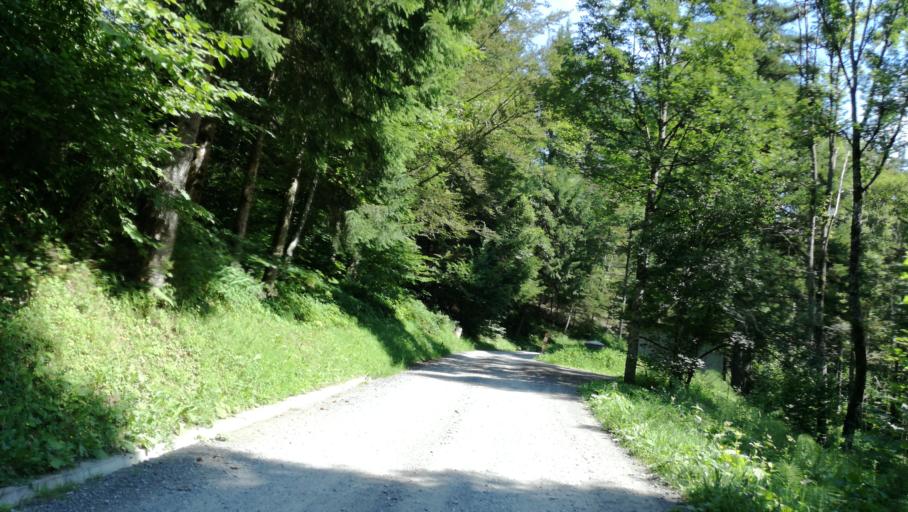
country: CH
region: Zug
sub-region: Zug
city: Unterageri
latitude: 47.1446
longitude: 8.5968
